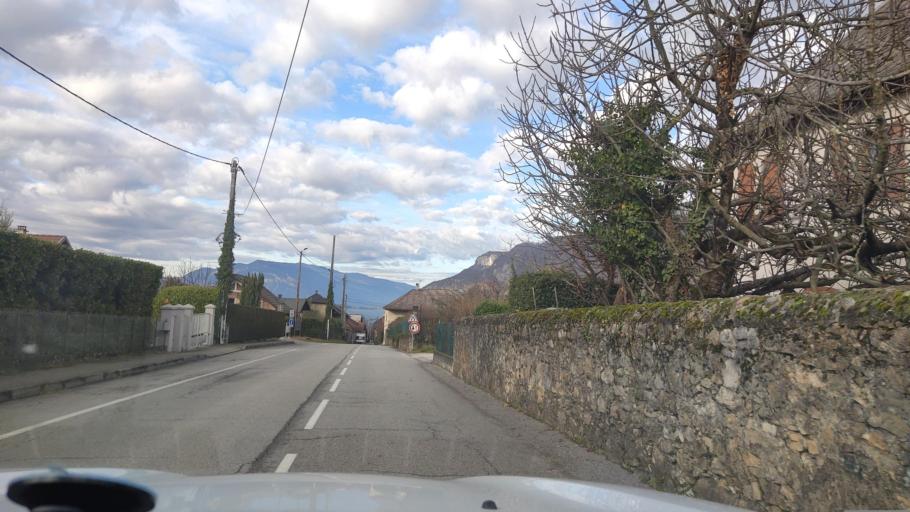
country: FR
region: Rhone-Alpes
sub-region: Departement de la Savoie
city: Brison-Saint-Innocent
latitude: 45.7285
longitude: 5.8869
